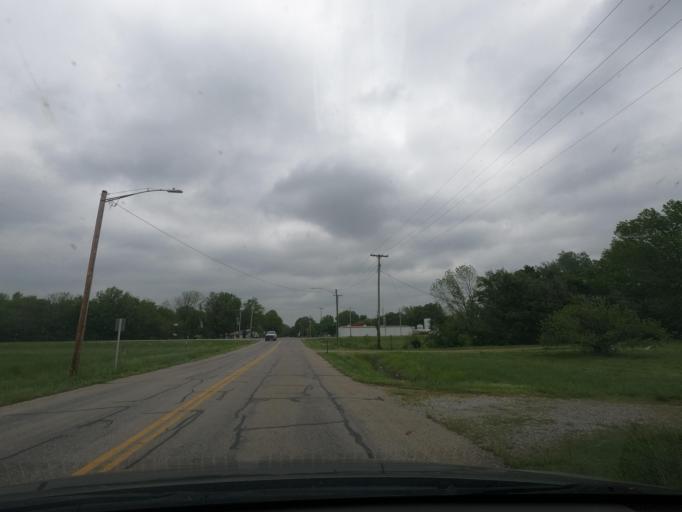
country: US
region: Kansas
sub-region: Cherokee County
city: Columbus
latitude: 37.1779
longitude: -94.8425
